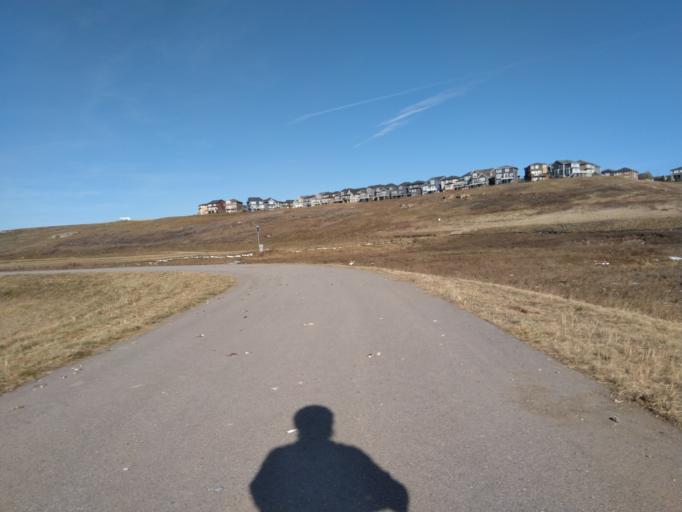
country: CA
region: Alberta
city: Calgary
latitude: 51.1786
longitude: -114.1296
